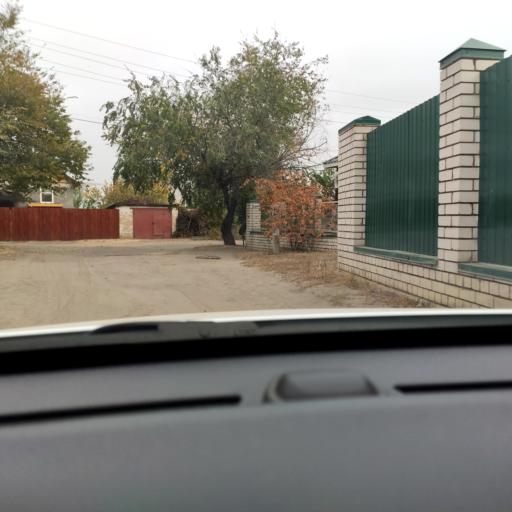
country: RU
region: Voronezj
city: Voronezh
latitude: 51.6970
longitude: 39.2639
